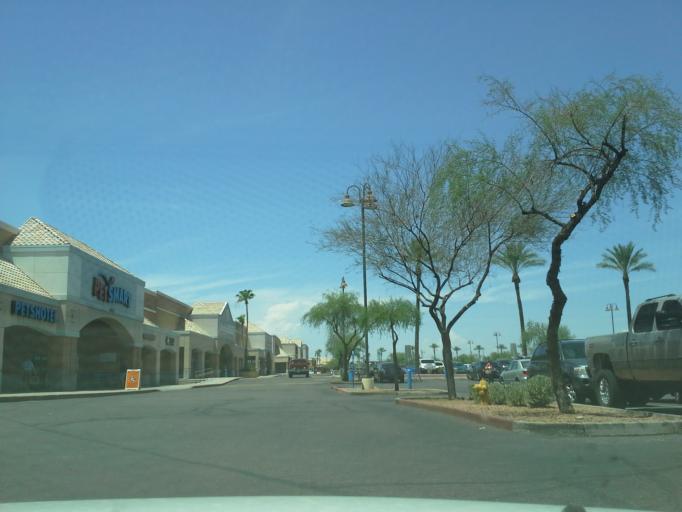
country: US
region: Arizona
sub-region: Maricopa County
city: Scottsdale
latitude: 33.5771
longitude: -111.8876
